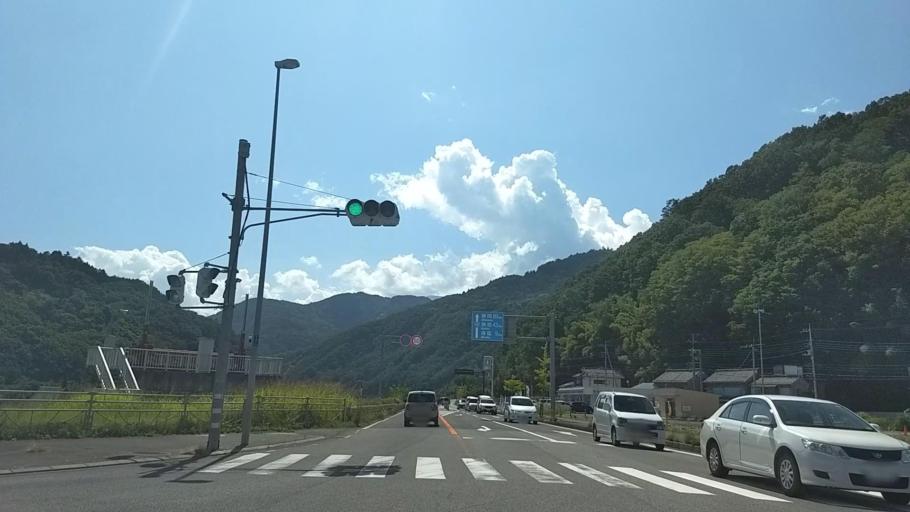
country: JP
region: Yamanashi
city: Ryuo
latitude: 35.5412
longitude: 138.4584
